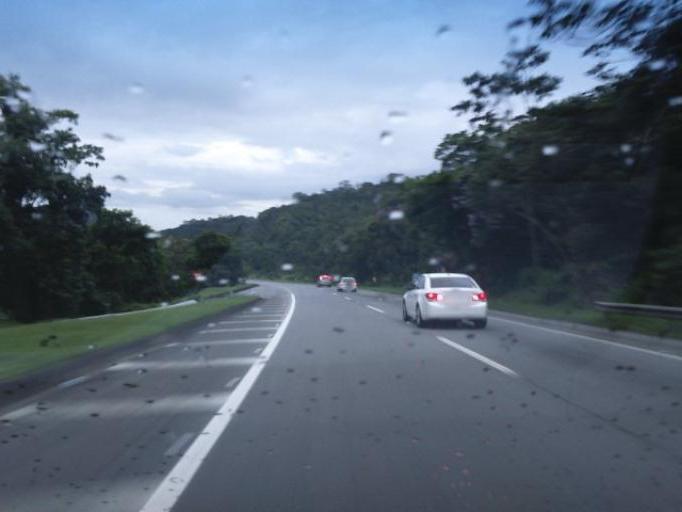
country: BR
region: Parana
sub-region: Guaratuba
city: Guaratuba
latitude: -25.9318
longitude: -48.9119
